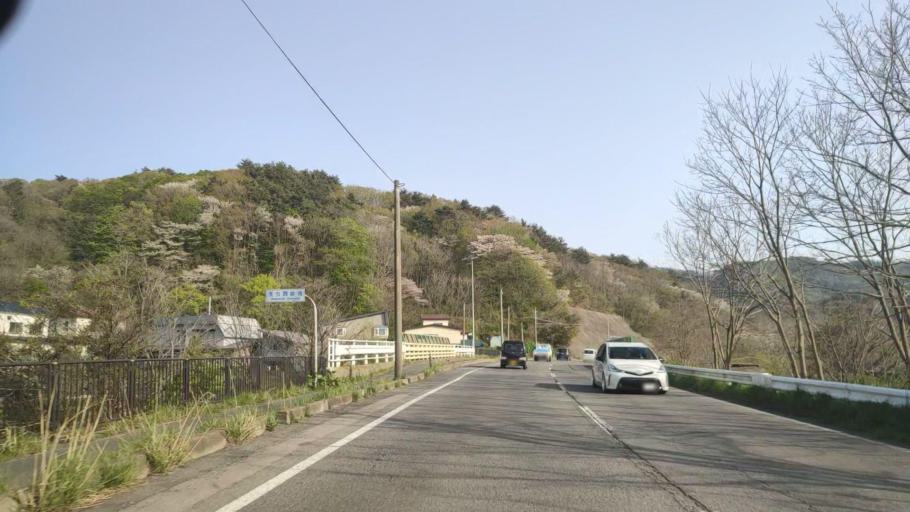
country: JP
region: Aomori
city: Aomori Shi
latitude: 40.8761
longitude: 140.8510
